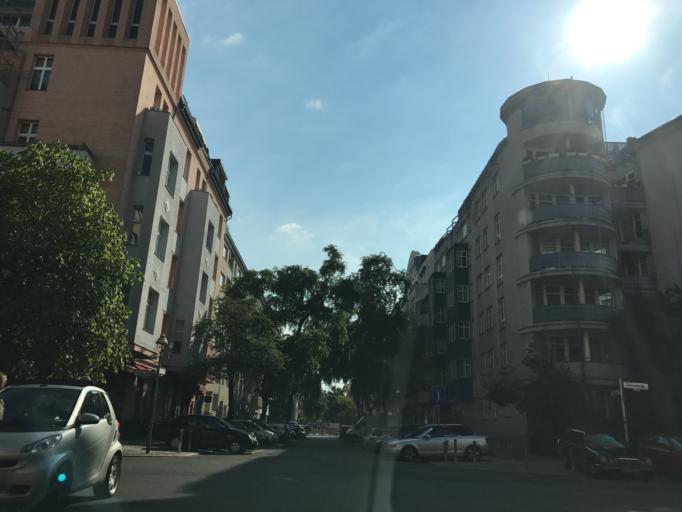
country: DE
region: Berlin
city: Halensee
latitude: 52.5020
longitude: 13.3036
